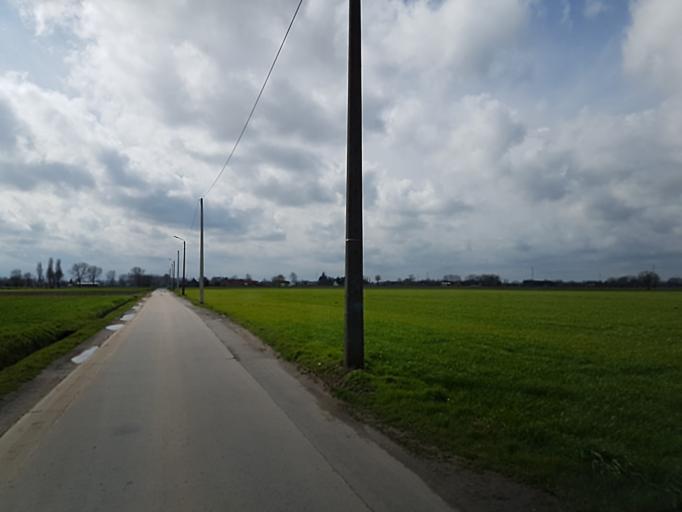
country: BE
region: Flanders
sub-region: Provincie Oost-Vlaanderen
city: Kruishoutem
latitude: 50.9333
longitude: 3.5042
